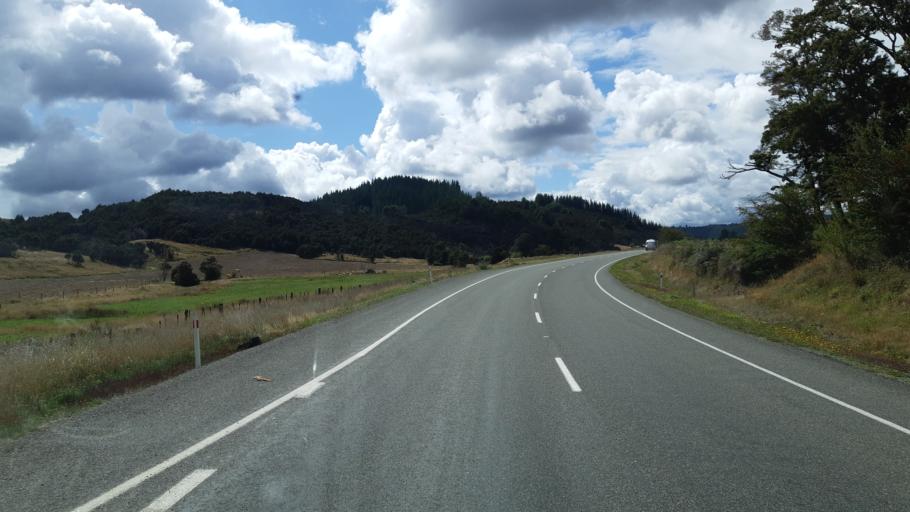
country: NZ
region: Tasman
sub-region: Tasman District
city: Wakefield
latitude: -41.6426
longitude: 172.6607
